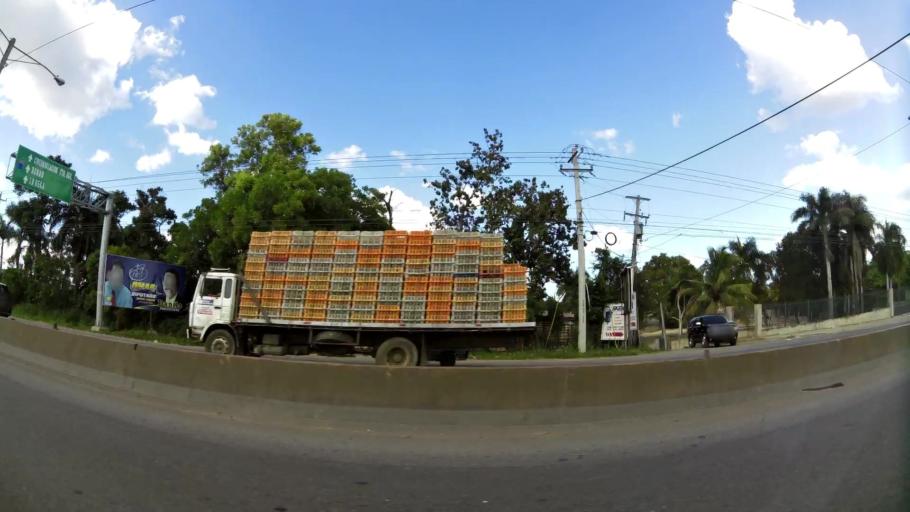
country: DO
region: Santo Domingo
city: Santo Domingo Oeste
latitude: 18.5398
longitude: -70.0308
